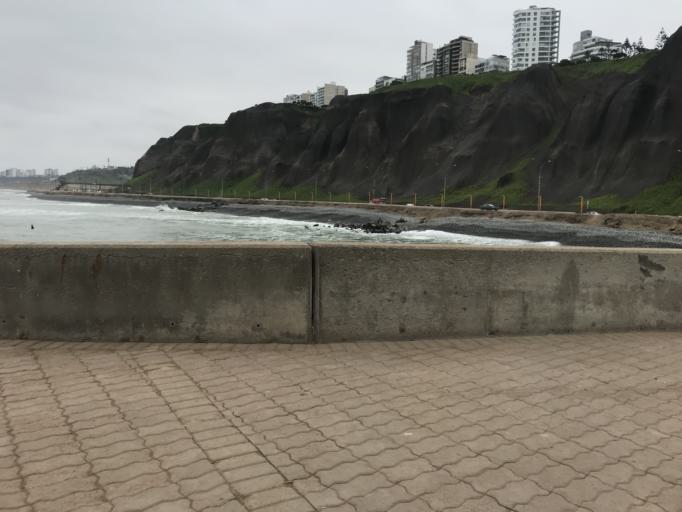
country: PE
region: Lima
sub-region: Lima
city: San Isidro
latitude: -12.1201
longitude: -77.0465
